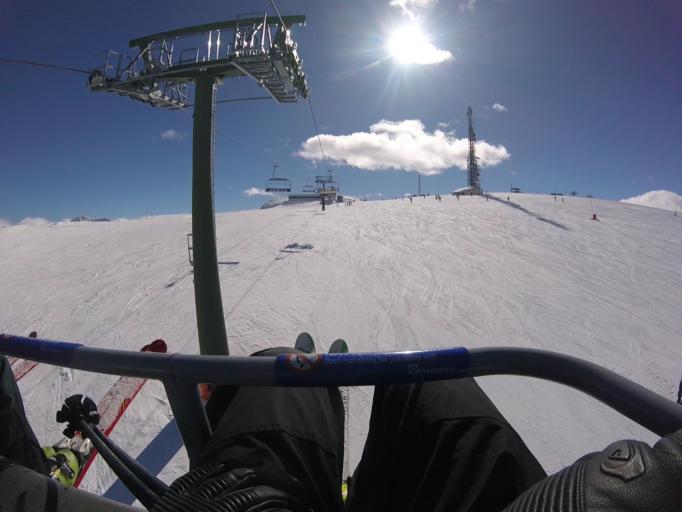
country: ES
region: Catalonia
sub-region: Provincia de Lleida
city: Espot
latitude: 42.6938
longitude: 0.9734
